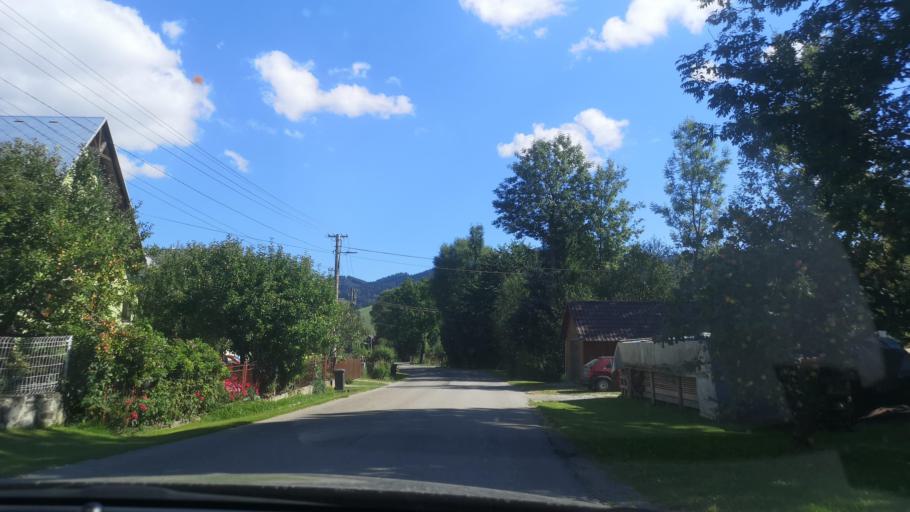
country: SK
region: Zilinsky
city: Oravska Lesna
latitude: 49.2748
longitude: 19.1379
